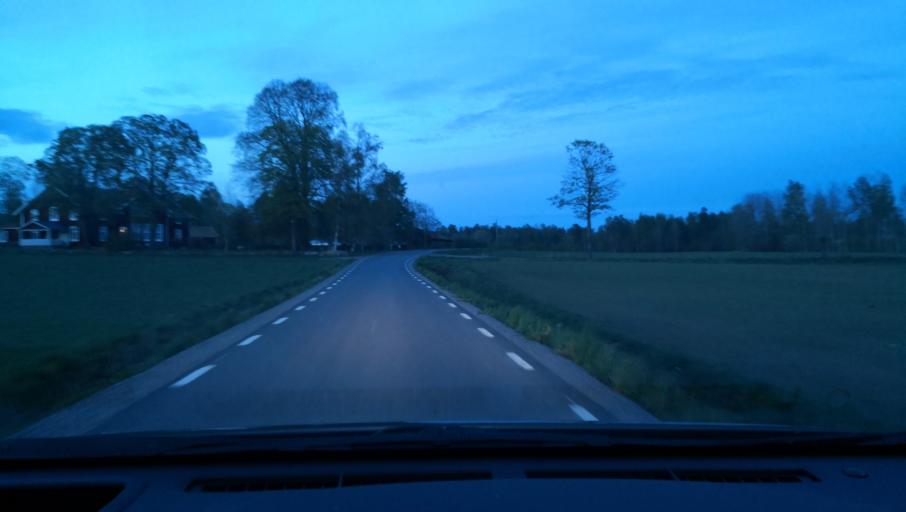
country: SE
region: OErebro
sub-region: Askersunds Kommun
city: Asbro
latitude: 59.0677
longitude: 14.9559
